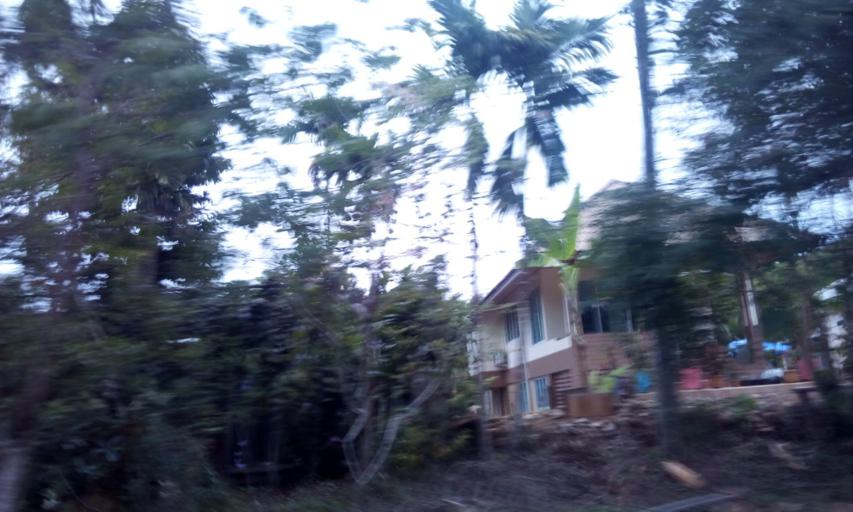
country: TH
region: Trat
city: Laem Ngop
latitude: 12.2217
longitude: 102.3078
